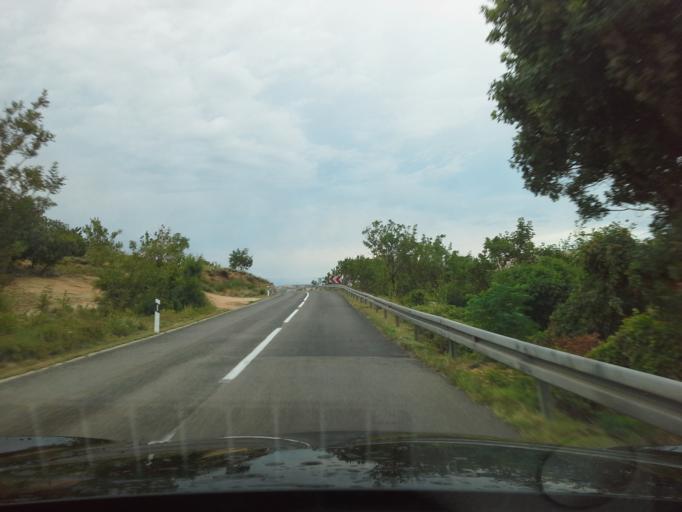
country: HR
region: Primorsko-Goranska
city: Banjol
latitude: 44.7137
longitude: 14.8280
